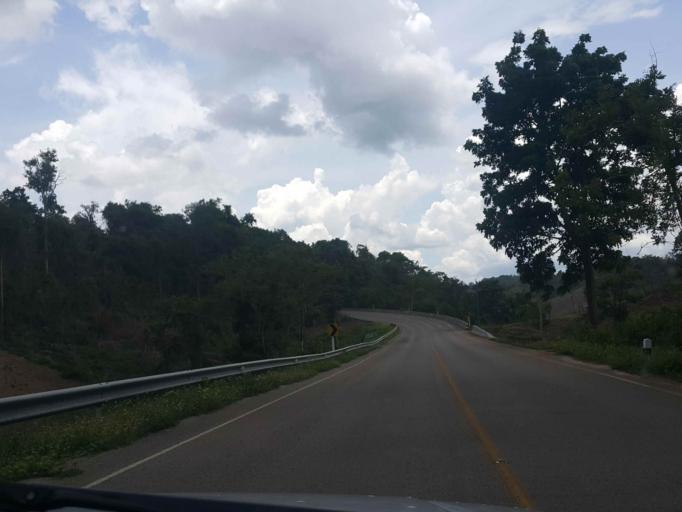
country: TH
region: Lampang
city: Ngao
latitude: 18.9313
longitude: 100.0905
